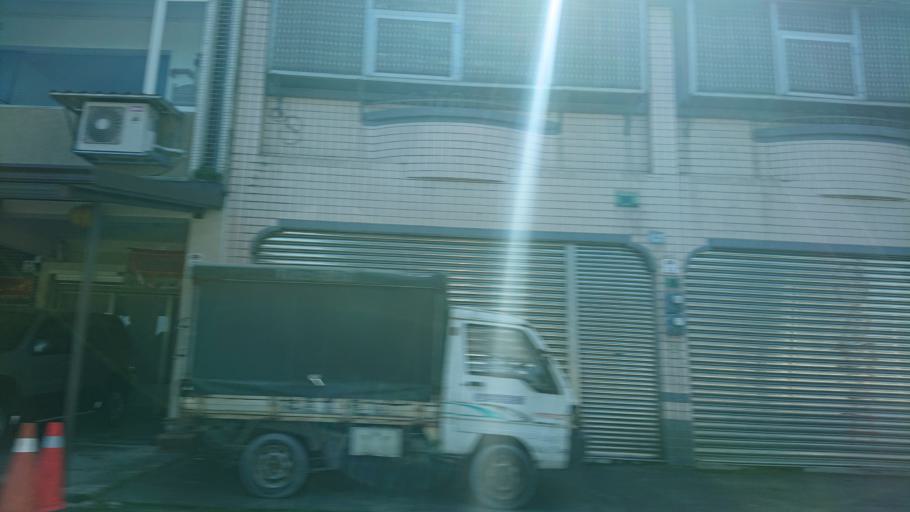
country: TW
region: Taiwan
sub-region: Yilan
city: Yilan
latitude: 24.6699
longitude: 121.7203
